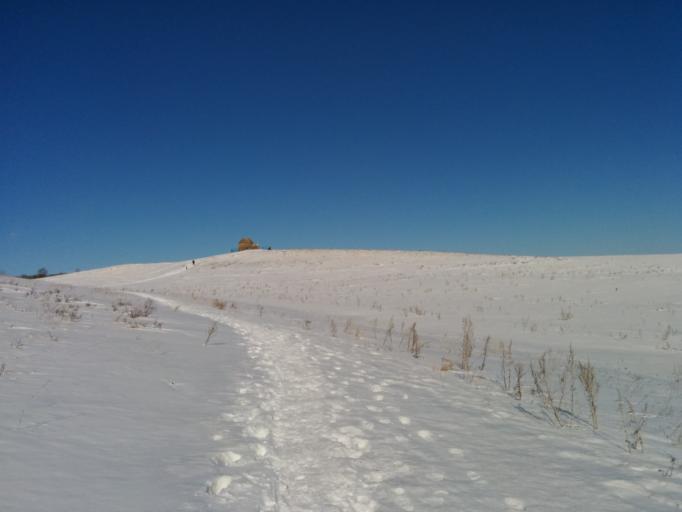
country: RU
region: Bashkortostan
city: Chishmy
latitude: 54.6027
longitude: 55.2165
